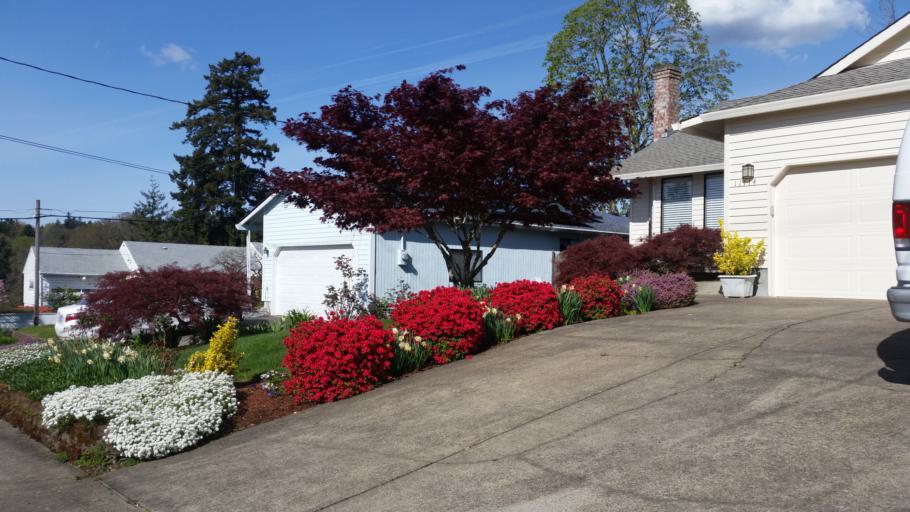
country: US
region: Oregon
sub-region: Washington County
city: Metzger
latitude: 45.4447
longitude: -122.7436
